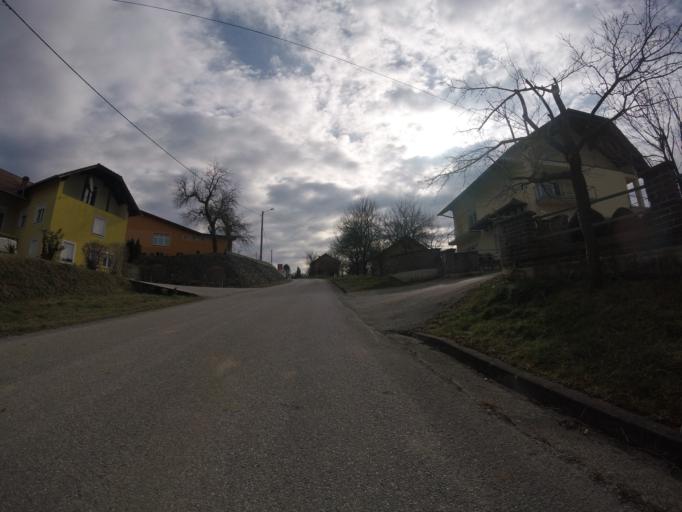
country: HR
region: Sisacko-Moslavacka
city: Glina
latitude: 45.4766
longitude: 16.0221
